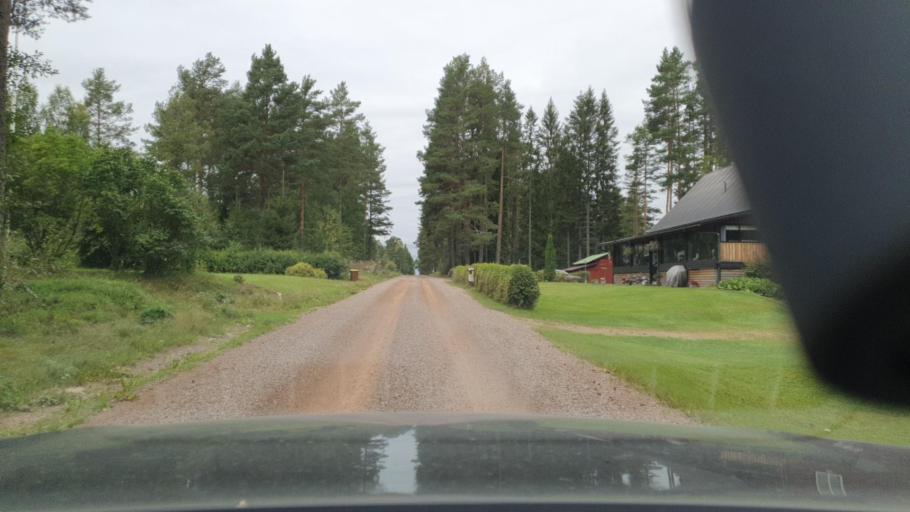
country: SE
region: Vaermland
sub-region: Eda Kommun
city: Charlottenberg
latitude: 60.0857
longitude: 12.5186
